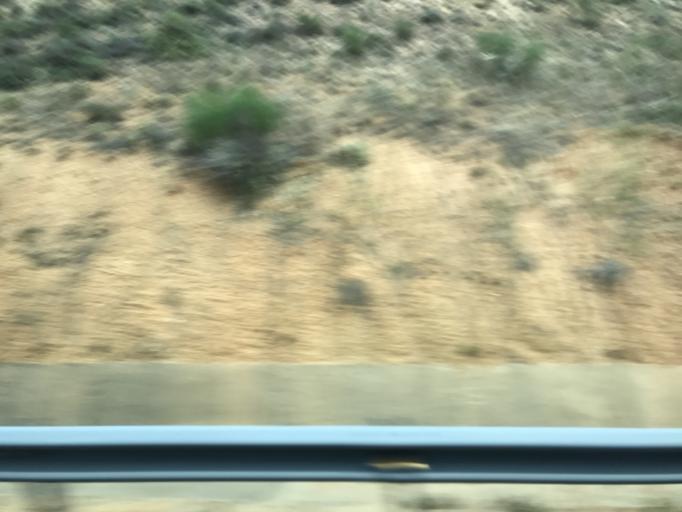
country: ES
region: Castille and Leon
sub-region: Provincia de Burgos
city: Bahabon de Esgueva
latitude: 41.8755
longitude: -3.7316
